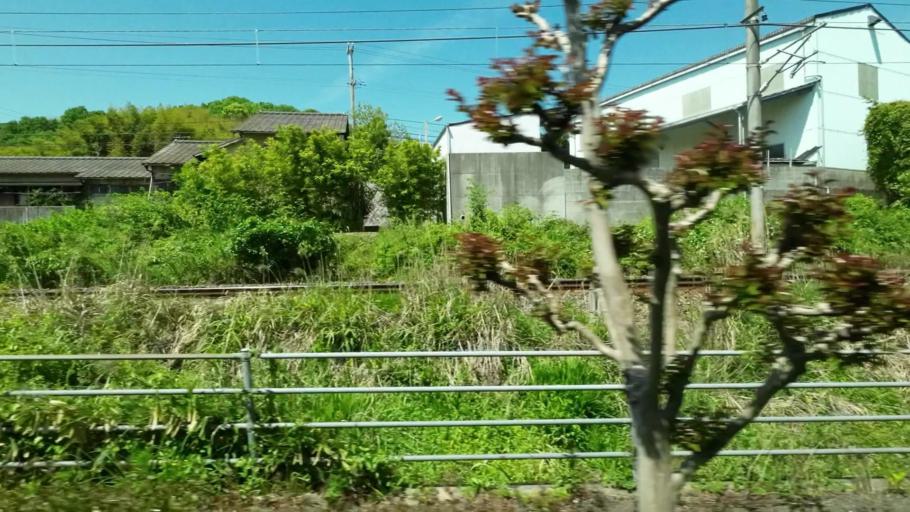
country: JP
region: Ehime
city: Hojo
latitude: 34.0829
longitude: 132.9844
